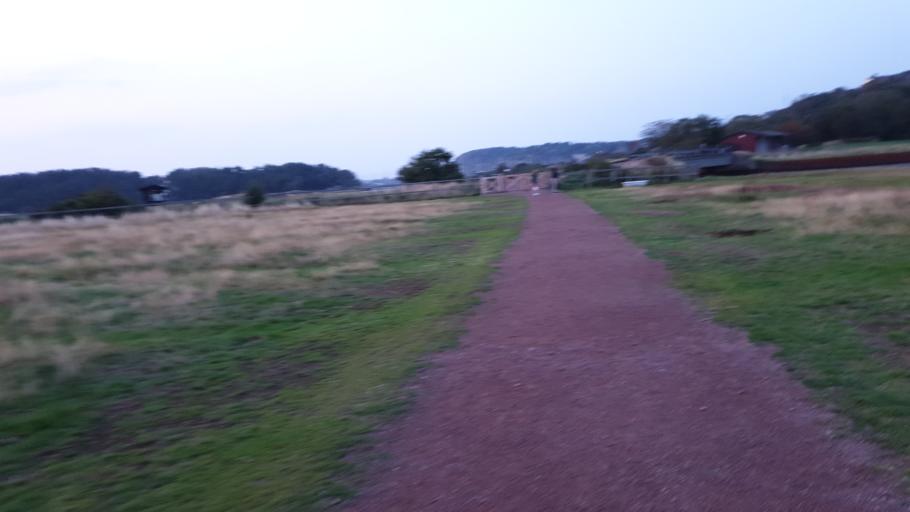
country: SE
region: Vaestra Goetaland
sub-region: Goteborg
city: Billdal
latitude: 57.5931
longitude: 11.9190
